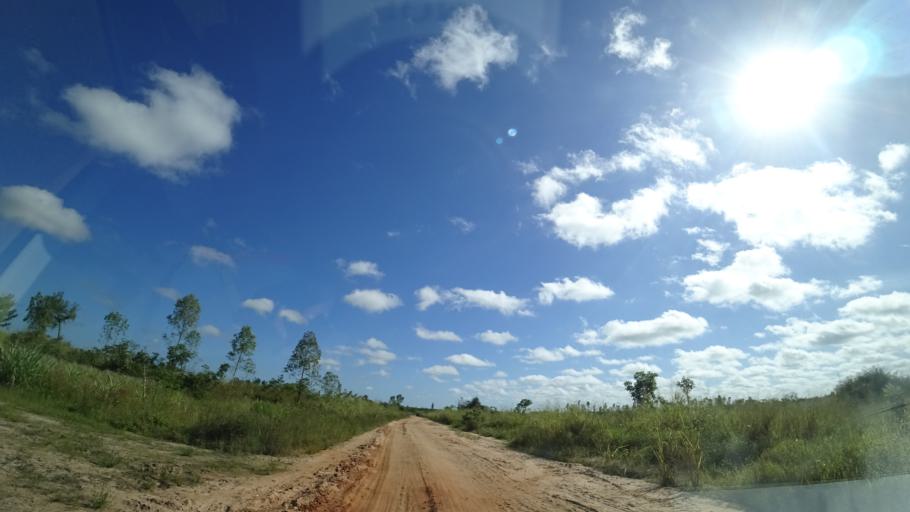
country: MZ
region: Sofala
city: Dondo
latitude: -19.4285
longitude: 34.7082
